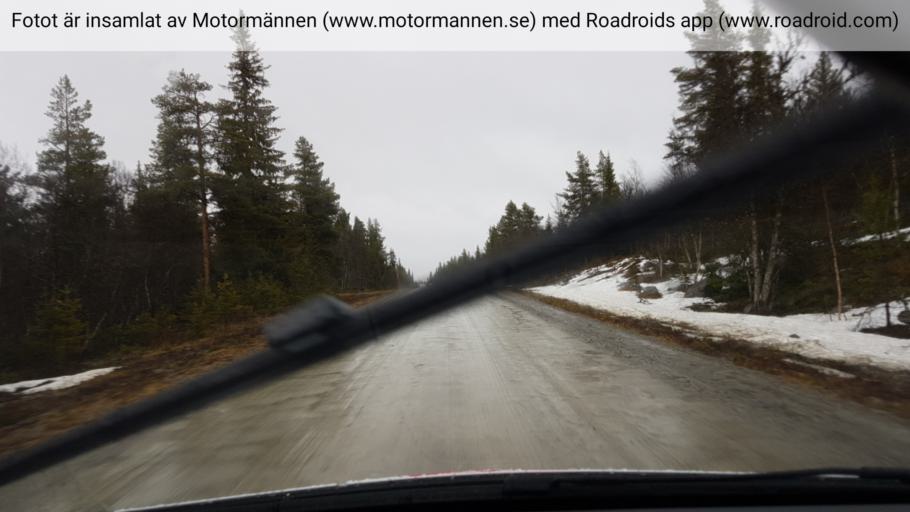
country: SE
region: Jaemtland
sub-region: Are Kommun
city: Are
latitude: 62.6593
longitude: 13.0178
